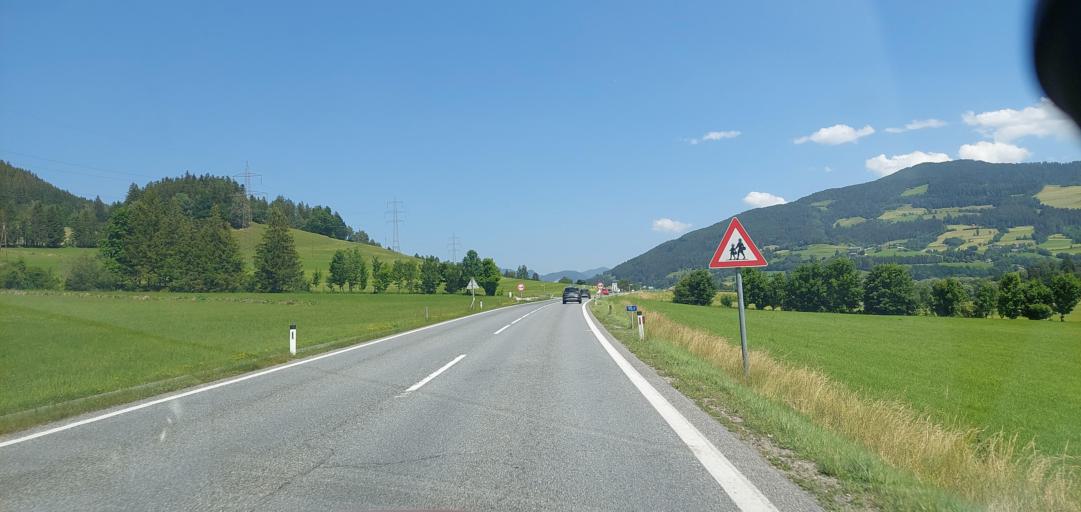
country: AT
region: Styria
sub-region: Politischer Bezirk Liezen
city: Sankt Martin am Grimming
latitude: 47.4867
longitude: 13.9927
